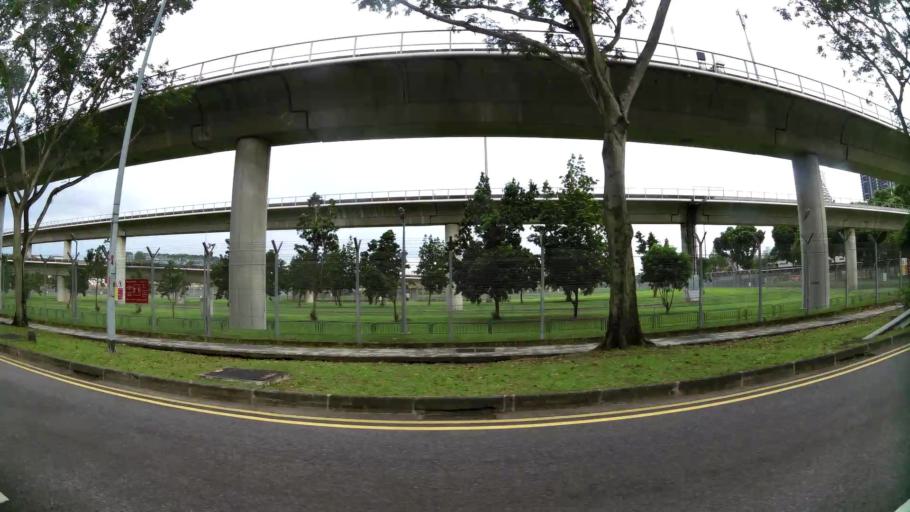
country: SG
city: Singapore
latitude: 1.3575
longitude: 103.8506
